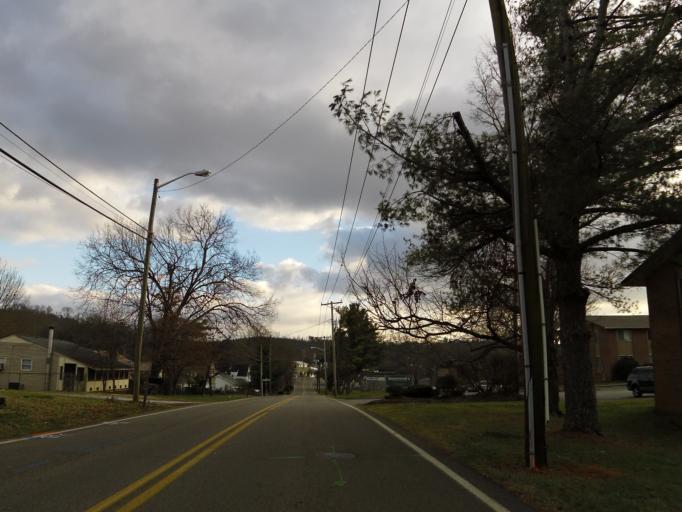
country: US
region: Tennessee
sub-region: Knox County
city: Knoxville
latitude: 35.9470
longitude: -83.8910
